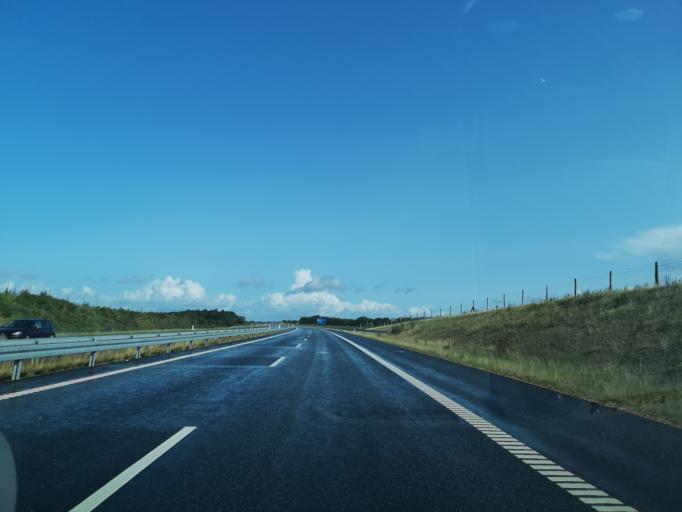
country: DK
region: Central Jutland
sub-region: Herning Kommune
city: Snejbjerg
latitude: 56.1747
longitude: 8.8923
